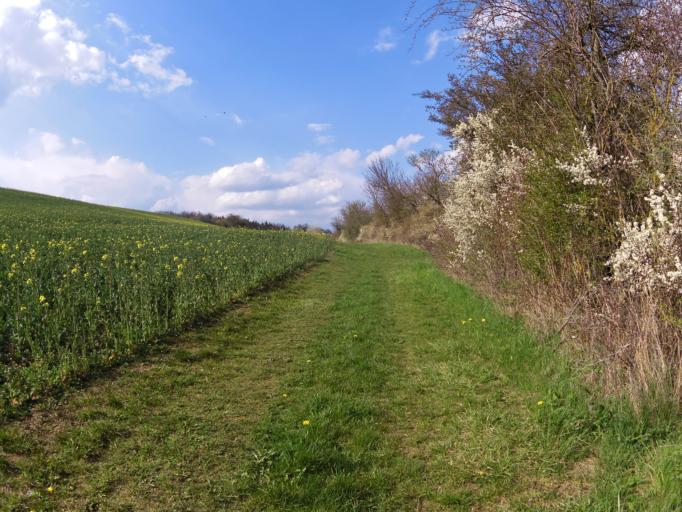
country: DE
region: Bavaria
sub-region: Regierungsbezirk Unterfranken
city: Rimpar
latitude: 49.8644
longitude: 9.9451
